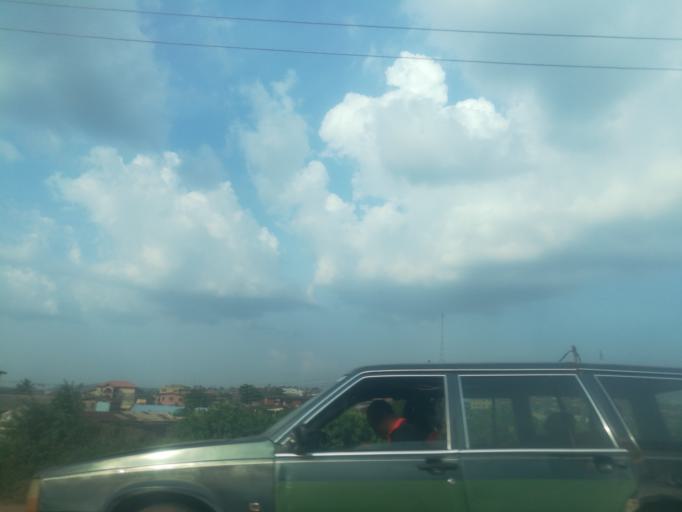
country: NG
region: Ogun
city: Abeokuta
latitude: 7.1472
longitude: 3.3268
